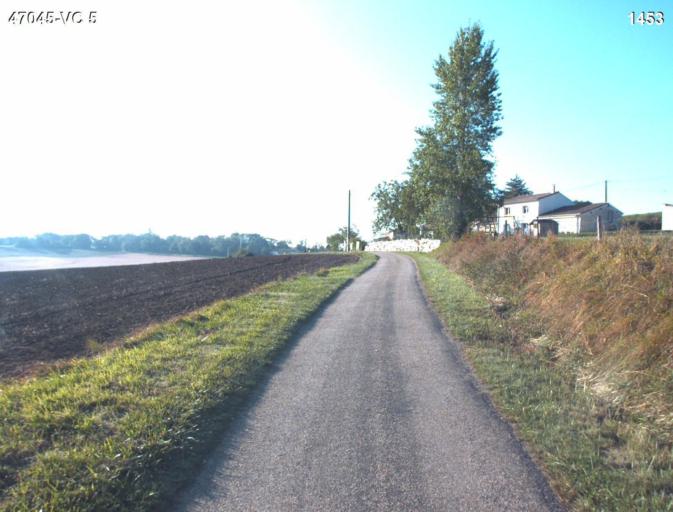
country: FR
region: Aquitaine
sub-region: Departement du Lot-et-Garonne
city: Nerac
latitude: 44.1423
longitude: 0.4050
